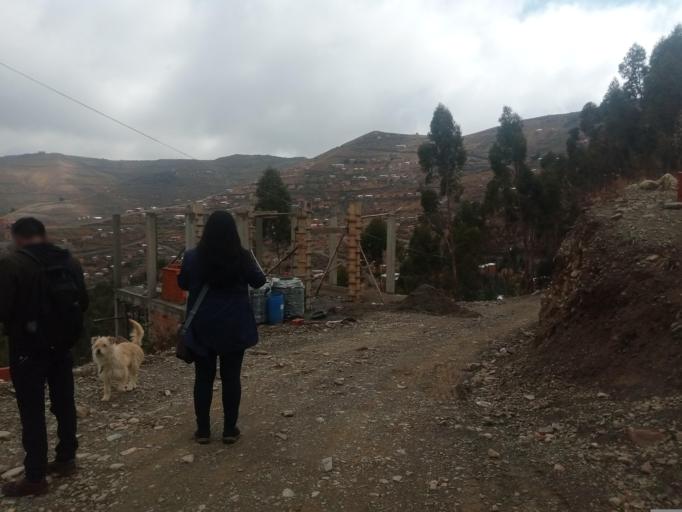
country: BO
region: La Paz
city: La Paz
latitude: -16.4649
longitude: -68.1431
